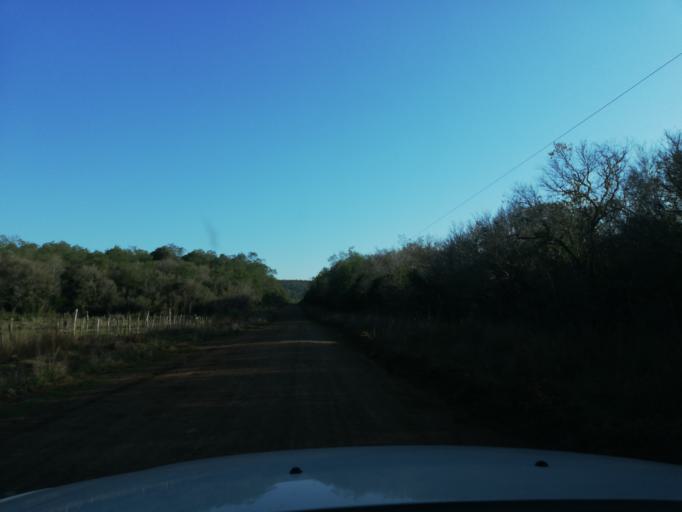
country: AR
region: Misiones
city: Cerro Cora
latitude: -27.6009
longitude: -55.6994
